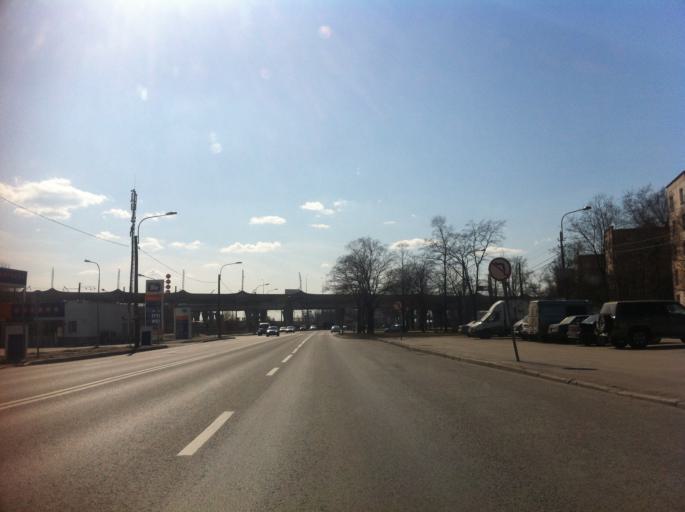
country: RU
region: St.-Petersburg
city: Dachnoye
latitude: 59.8376
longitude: 30.2703
